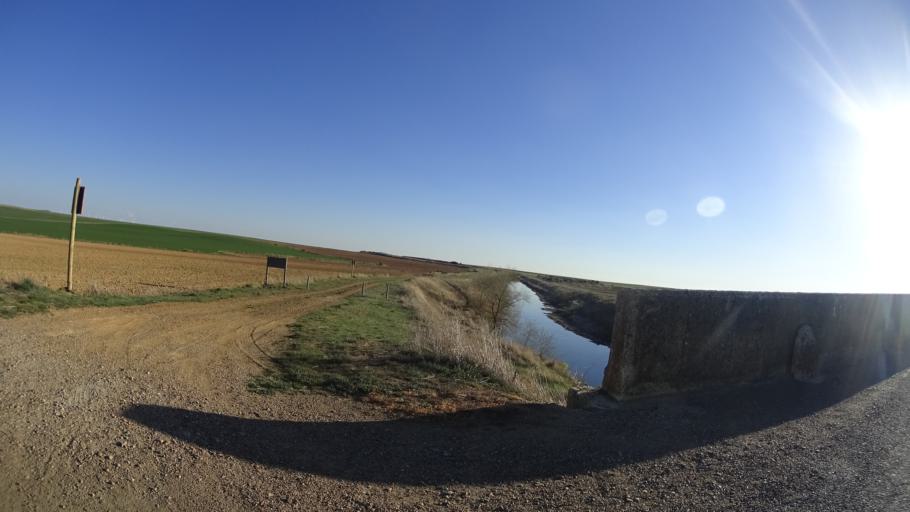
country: ES
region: Castille and Leon
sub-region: Provincia de Palencia
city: Requena de Campos
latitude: 42.3060
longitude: -4.3377
